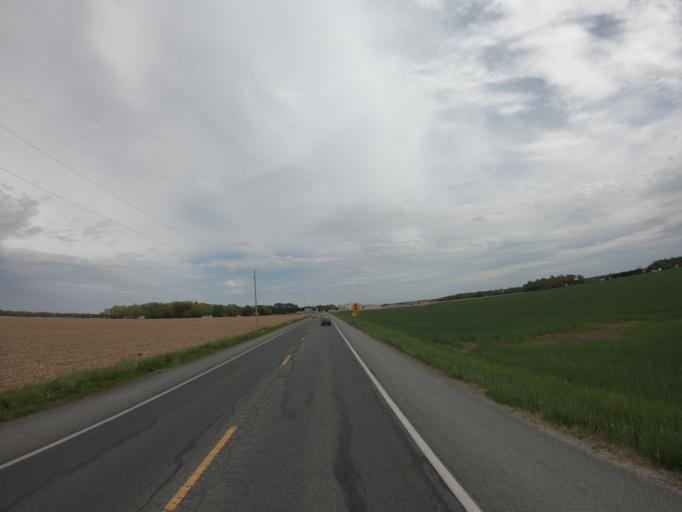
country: US
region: Delaware
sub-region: Sussex County
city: Milton
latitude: 38.7862
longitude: -75.3449
